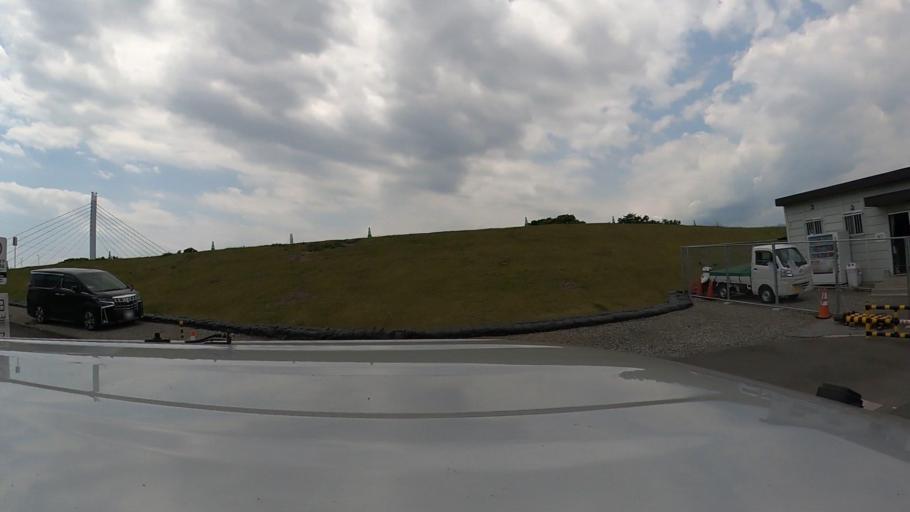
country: JP
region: Kanagawa
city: Chigasaki
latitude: 35.3551
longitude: 139.3732
